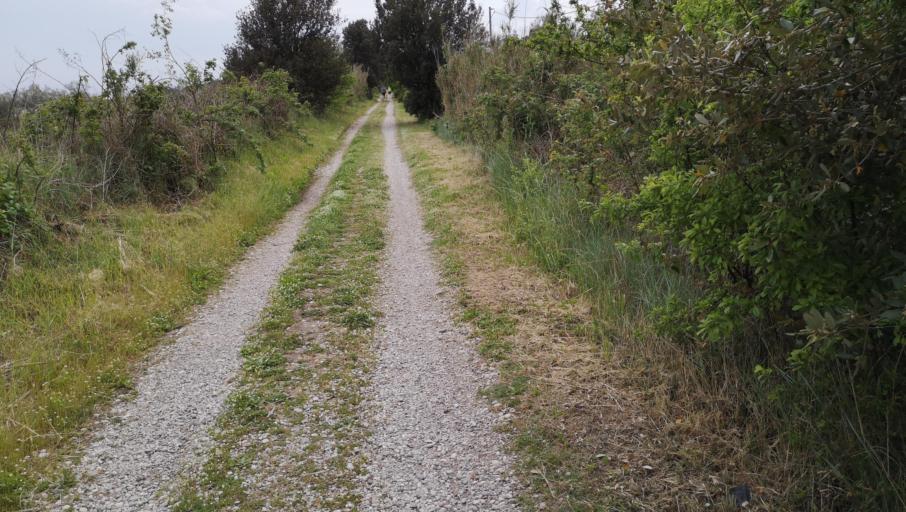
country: IT
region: Emilia-Romagna
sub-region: Provincia di Ferrara
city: Goro
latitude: 44.8275
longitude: 12.2691
